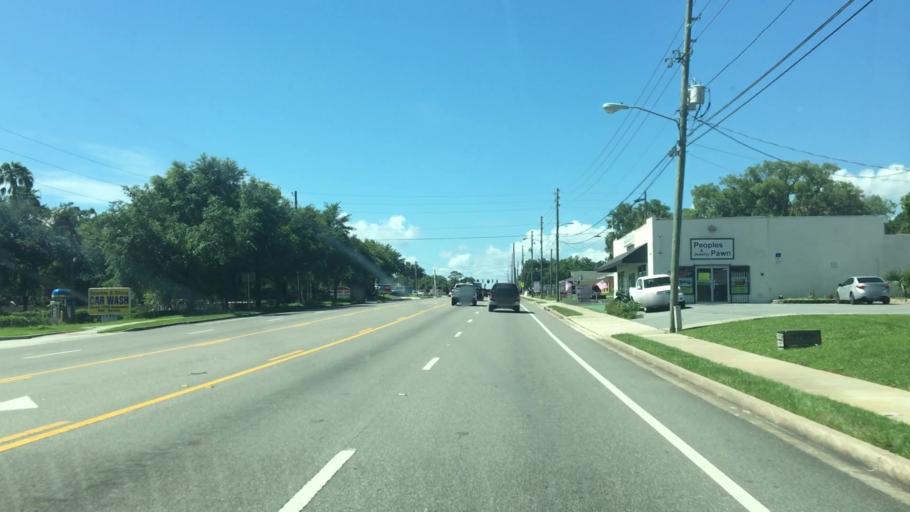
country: US
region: Florida
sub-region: Volusia County
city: Orange City
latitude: 28.9372
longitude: -81.2990
